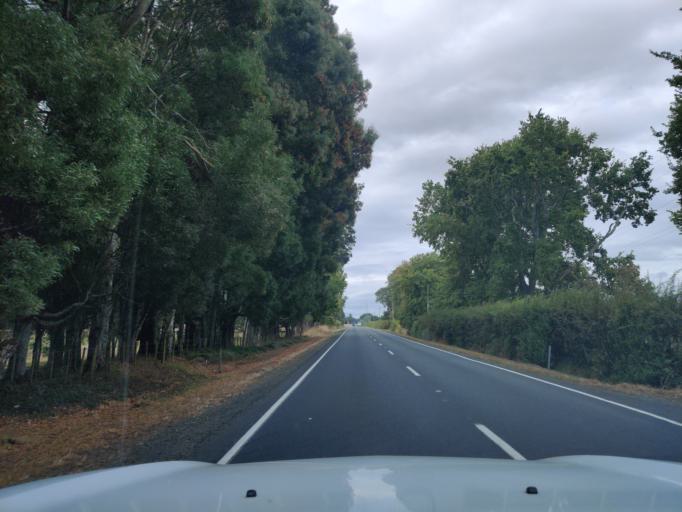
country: NZ
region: Waikato
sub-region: Waipa District
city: Cambridge
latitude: -37.8500
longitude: 175.4535
